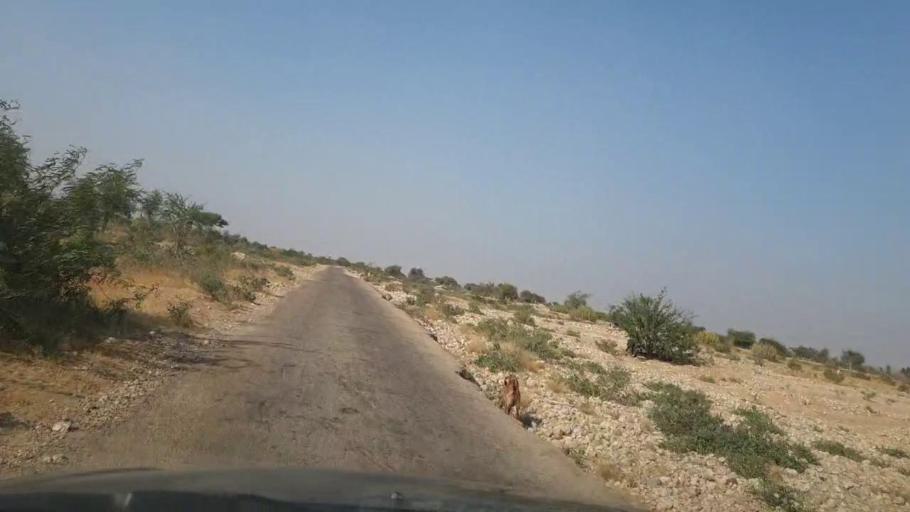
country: PK
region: Sindh
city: Jamshoro
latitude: 25.5679
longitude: 67.8246
